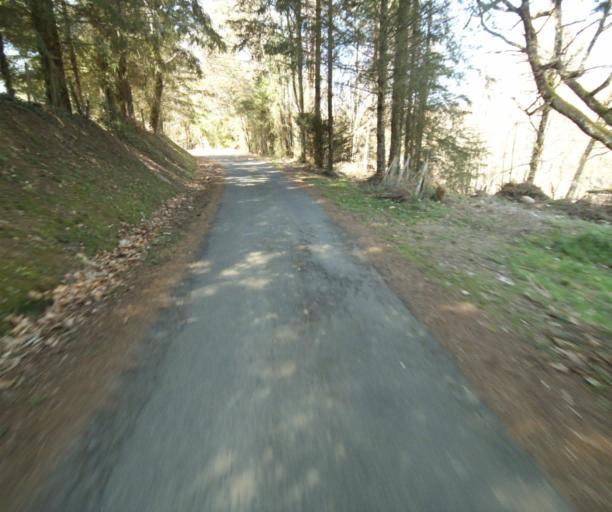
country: FR
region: Limousin
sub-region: Departement de la Correze
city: Chameyrat
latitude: 45.2776
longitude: 1.7037
